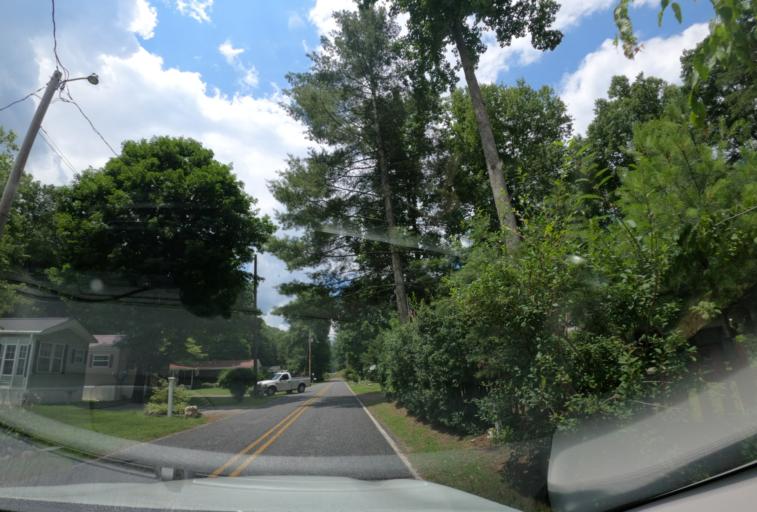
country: US
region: North Carolina
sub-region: Haywood County
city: Waynesville
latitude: 35.4095
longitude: -82.9033
